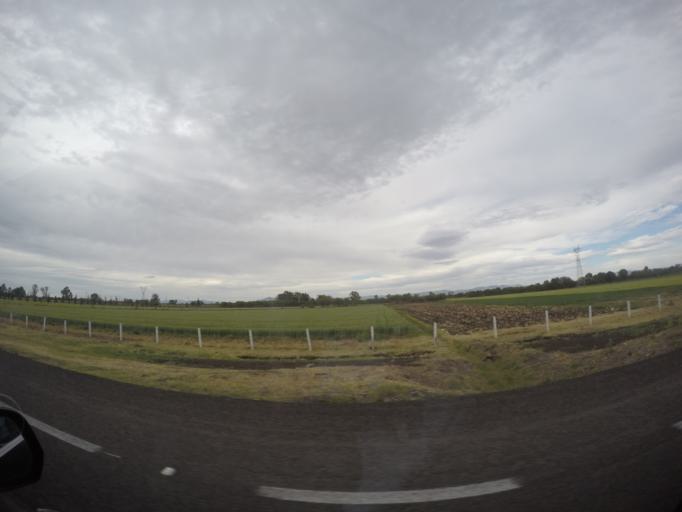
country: MX
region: Guanajuato
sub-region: Irapuato
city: Serrano
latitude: 20.7925
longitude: -101.4236
